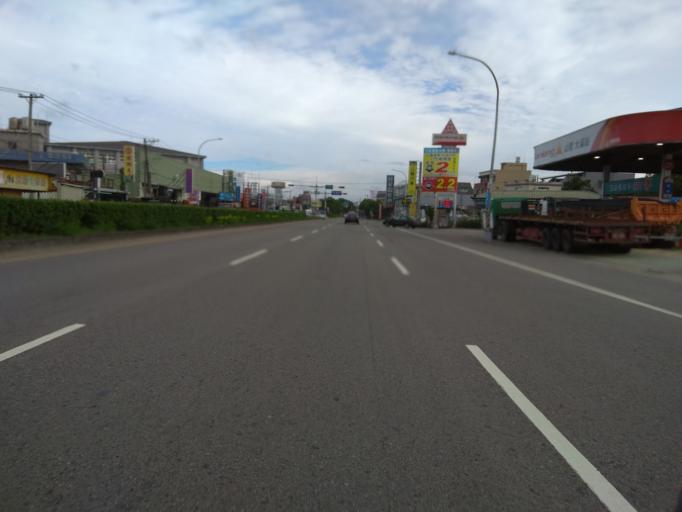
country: TW
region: Taiwan
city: Daxi
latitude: 24.9011
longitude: 121.2640
